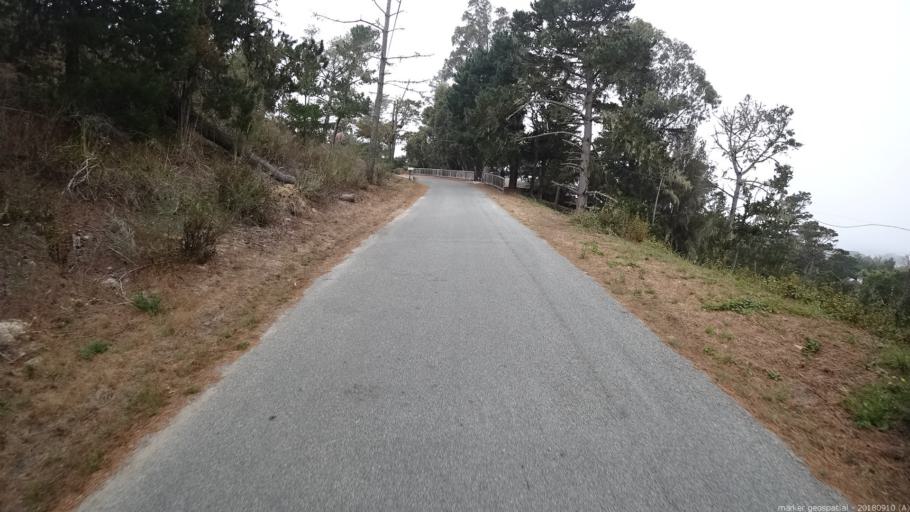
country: US
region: California
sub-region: Monterey County
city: Carmel-by-the-Sea
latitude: 36.4868
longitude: -121.9348
